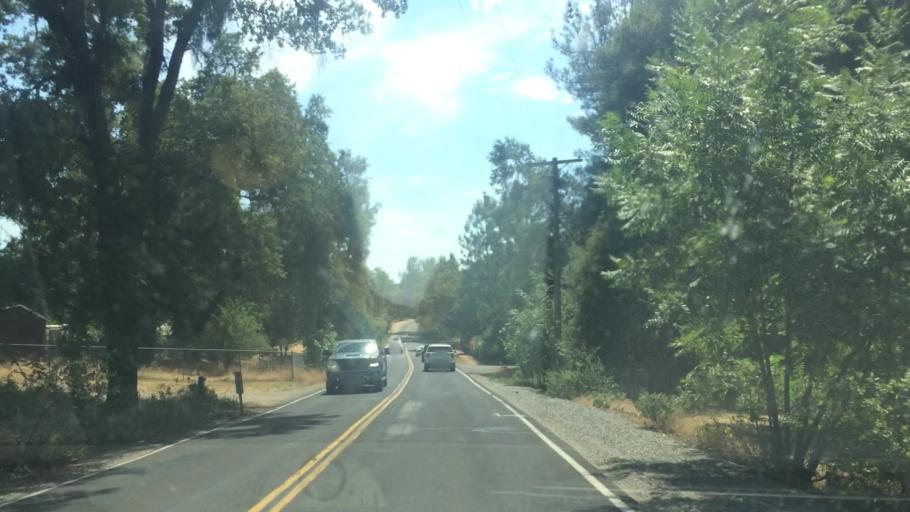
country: US
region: California
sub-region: Amador County
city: Pine Grove
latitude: 38.4086
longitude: -120.7110
